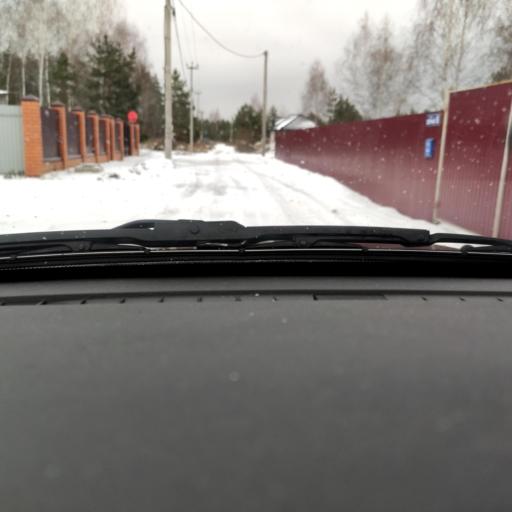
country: RU
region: Voronezj
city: Ramon'
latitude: 51.8946
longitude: 39.2576
